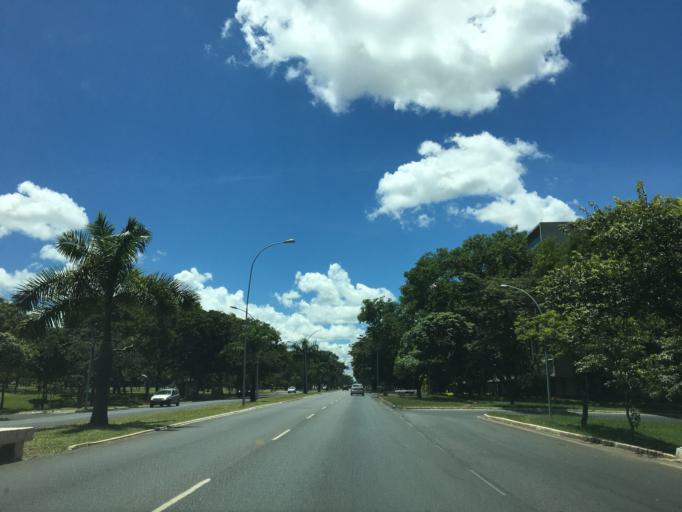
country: BR
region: Federal District
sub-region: Brasilia
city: Brasilia
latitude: -15.8296
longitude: -47.9171
